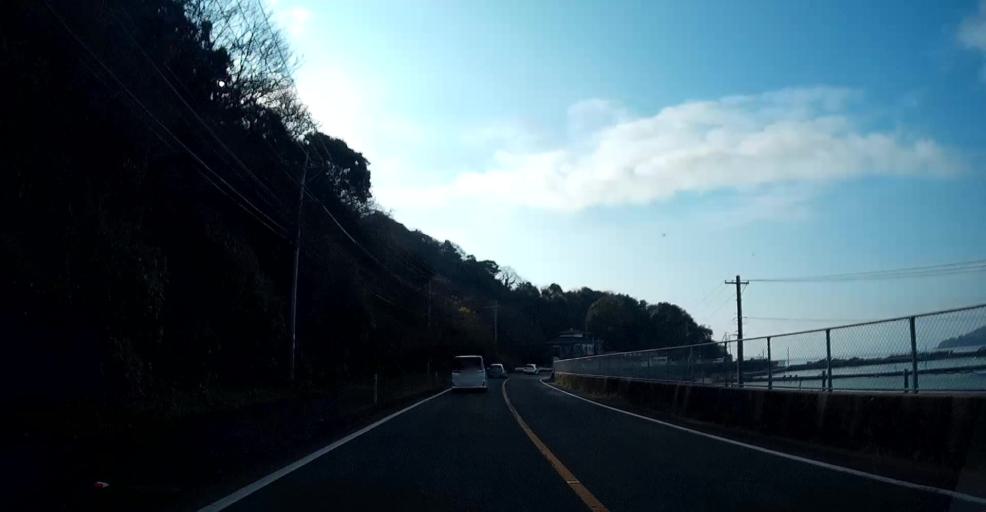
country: JP
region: Kumamoto
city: Yatsushiro
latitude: 32.5683
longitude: 130.4140
